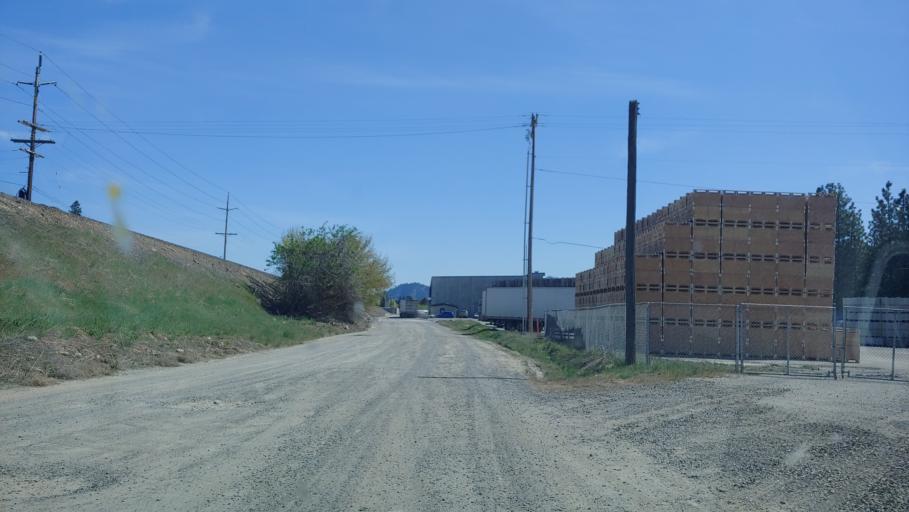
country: US
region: Washington
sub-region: Chelan County
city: Leavenworth
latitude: 47.5743
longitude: -120.6082
